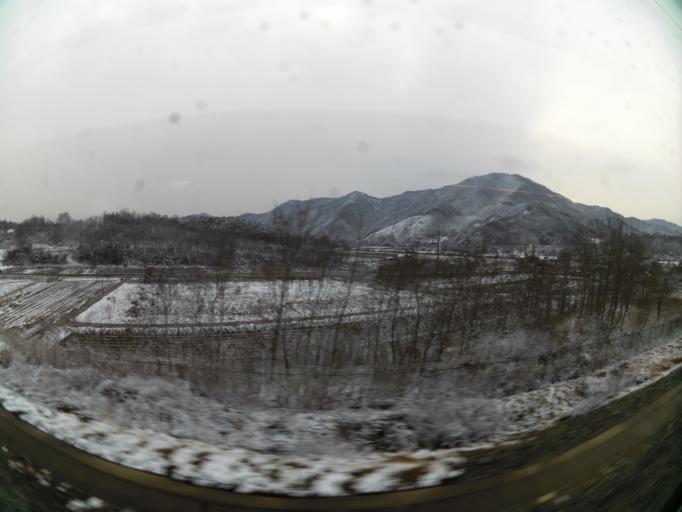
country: KR
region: Chungcheongbuk-do
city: Yong-dong
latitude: 36.2414
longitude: 127.6743
